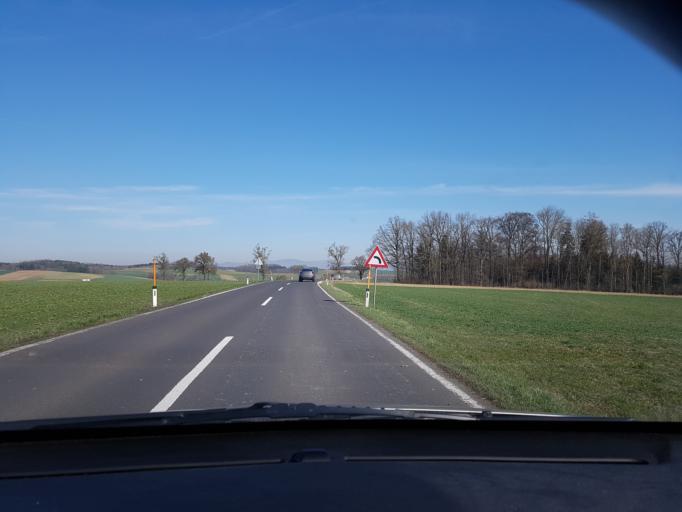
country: AT
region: Upper Austria
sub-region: Politischer Bezirk Linz-Land
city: Ansfelden
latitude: 48.1633
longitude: 14.3069
